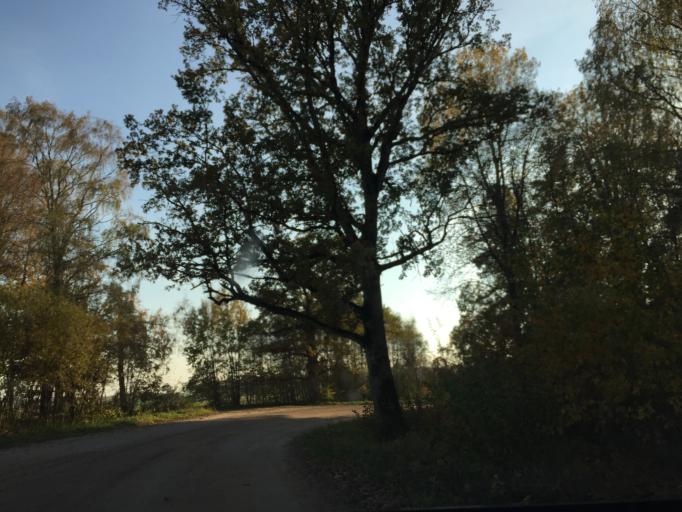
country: LV
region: Vainode
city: Vainode
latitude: 56.6200
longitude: 21.8175
